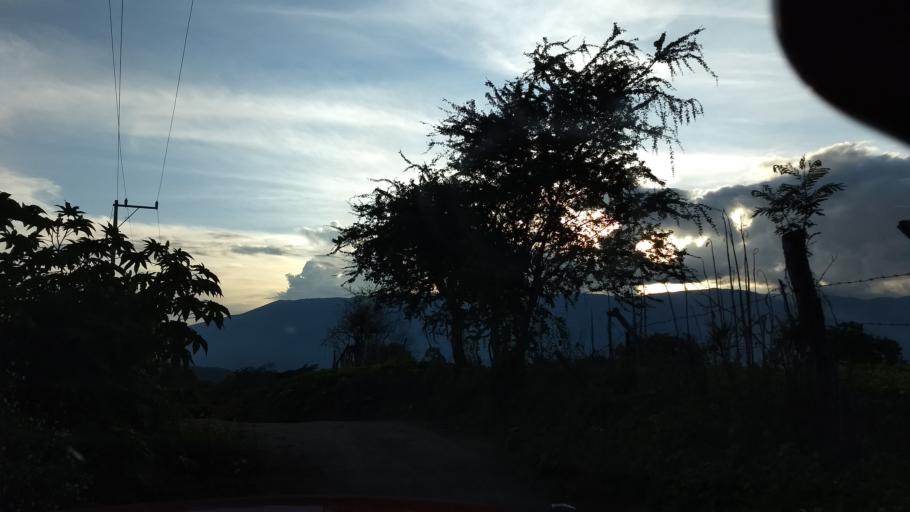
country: MX
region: Jalisco
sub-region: San Gabriel
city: Alista
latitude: 19.5013
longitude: -103.7655
